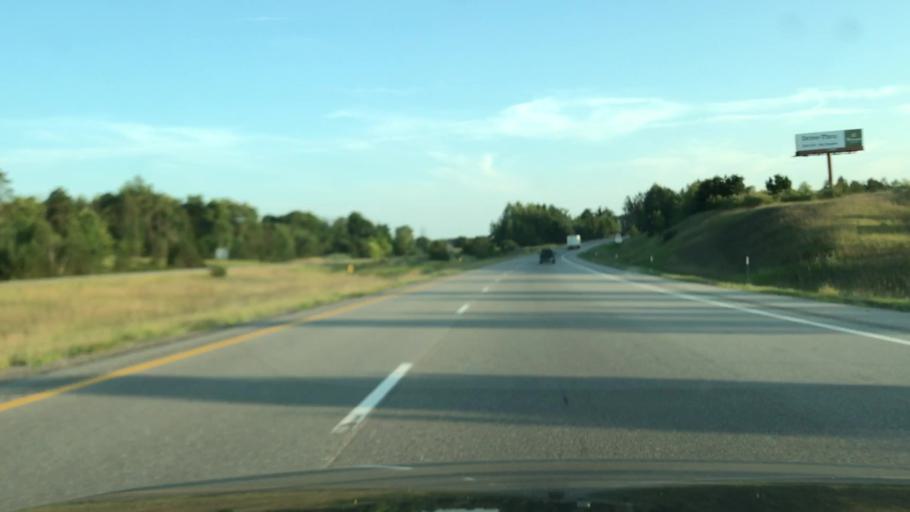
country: US
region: Michigan
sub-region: Osceola County
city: Reed City
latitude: 43.8797
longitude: -85.5282
